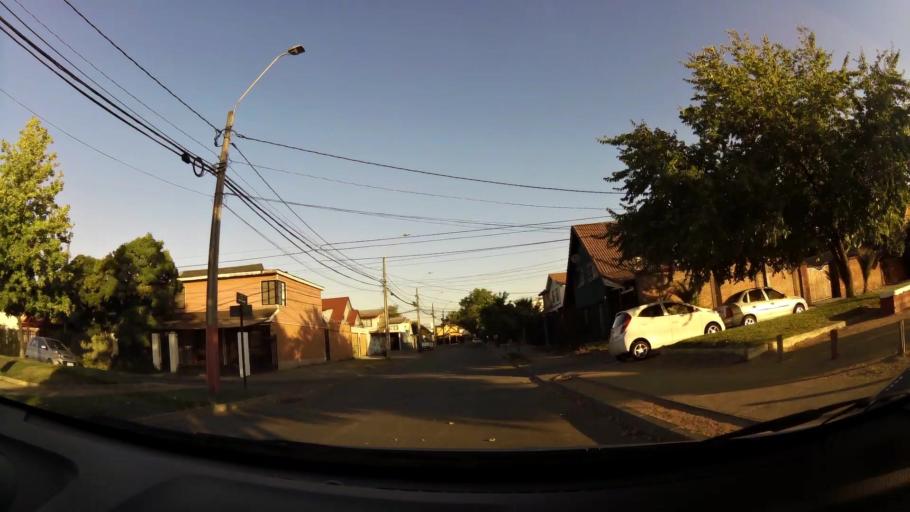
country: CL
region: Maule
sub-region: Provincia de Talca
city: Talca
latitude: -35.4465
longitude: -71.6881
